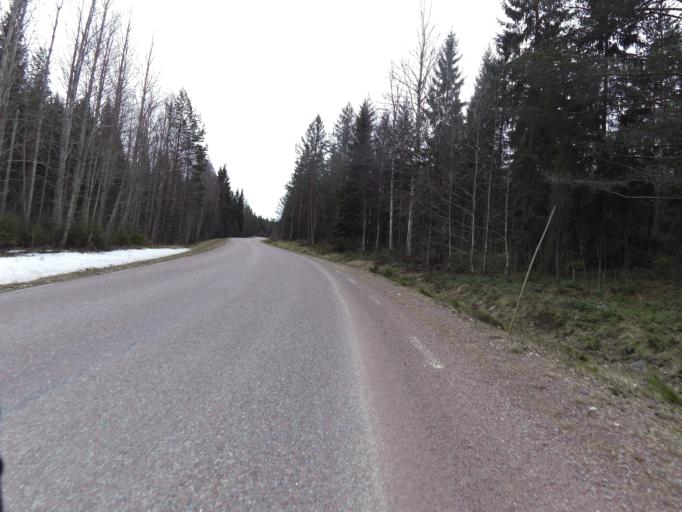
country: SE
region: Gaevleborg
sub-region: Hofors Kommun
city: Hofors
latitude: 60.4868
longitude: 16.4168
